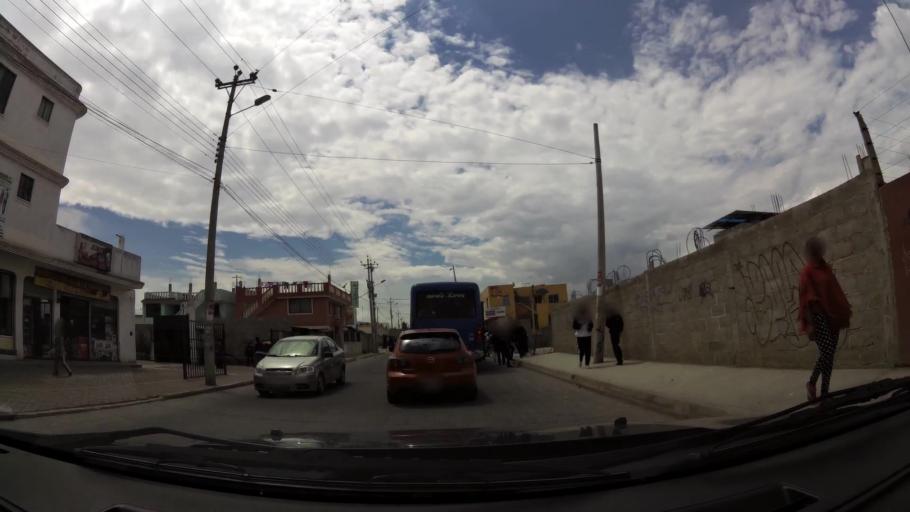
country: EC
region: Pichincha
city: Quito
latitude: -0.0776
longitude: -78.4172
